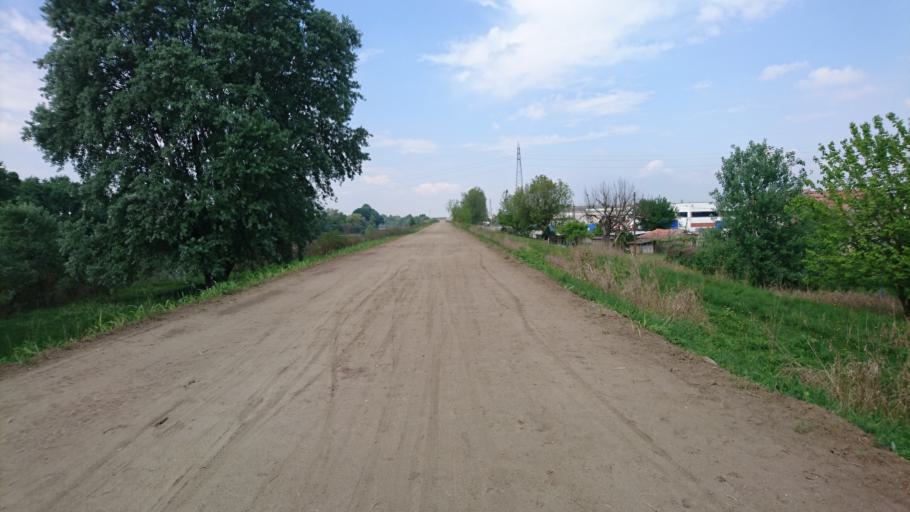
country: IT
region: Veneto
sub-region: Provincia di Padova
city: Oltre Brenta
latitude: 45.4165
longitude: 11.9869
